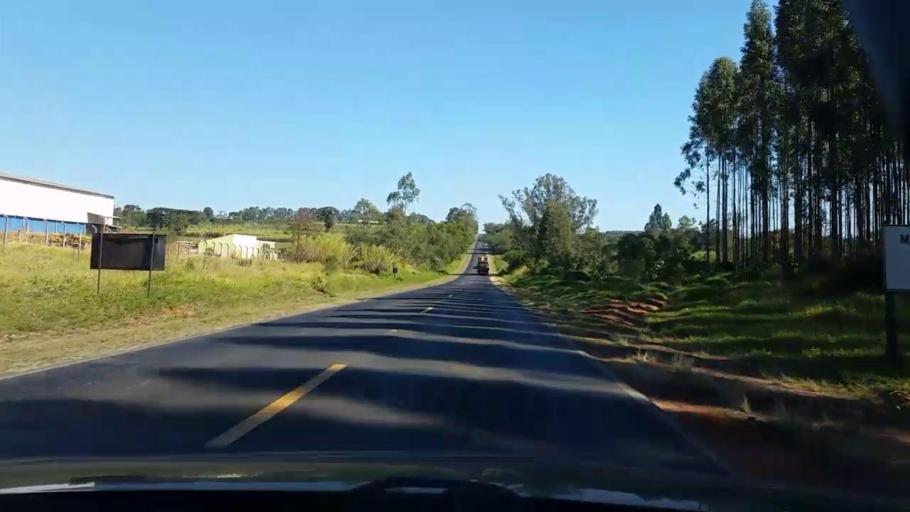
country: BR
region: Sao Paulo
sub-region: Sao Manuel
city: Sao Manuel
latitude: -22.8086
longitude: -48.6740
